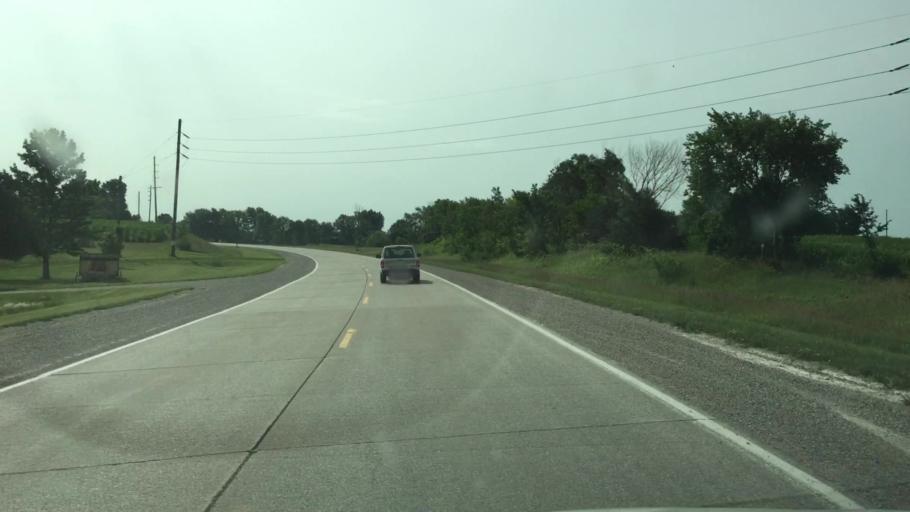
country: US
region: Illinois
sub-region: Hancock County
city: Nauvoo
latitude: 40.6333
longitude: -91.5148
